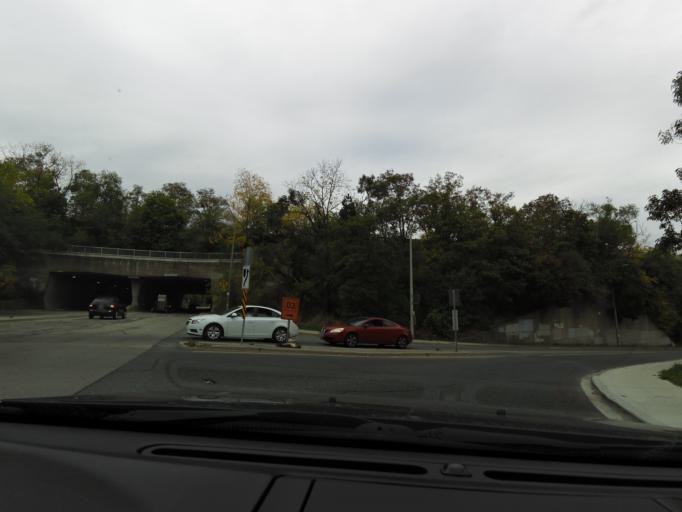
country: CA
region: Ontario
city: Hamilton
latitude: 43.2468
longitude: -79.8592
